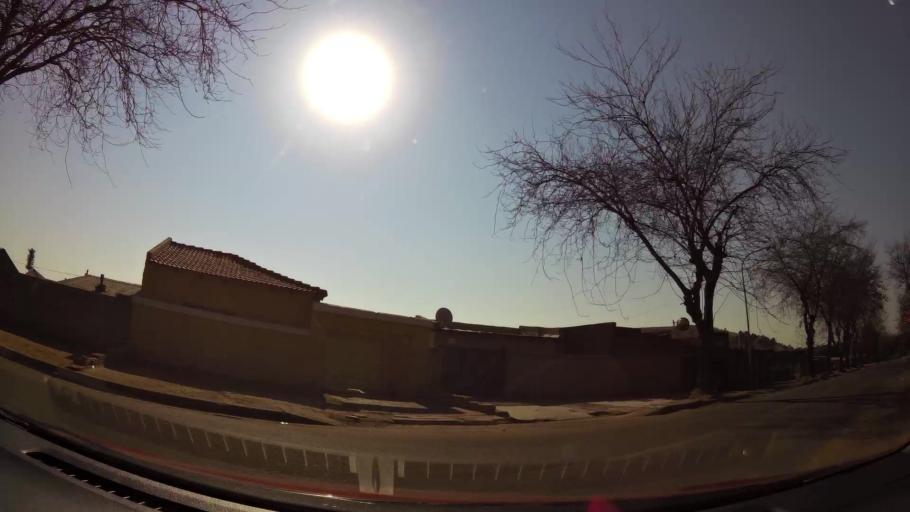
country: ZA
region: Gauteng
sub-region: City of Johannesburg Metropolitan Municipality
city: Johannesburg
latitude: -26.2455
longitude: 27.9597
